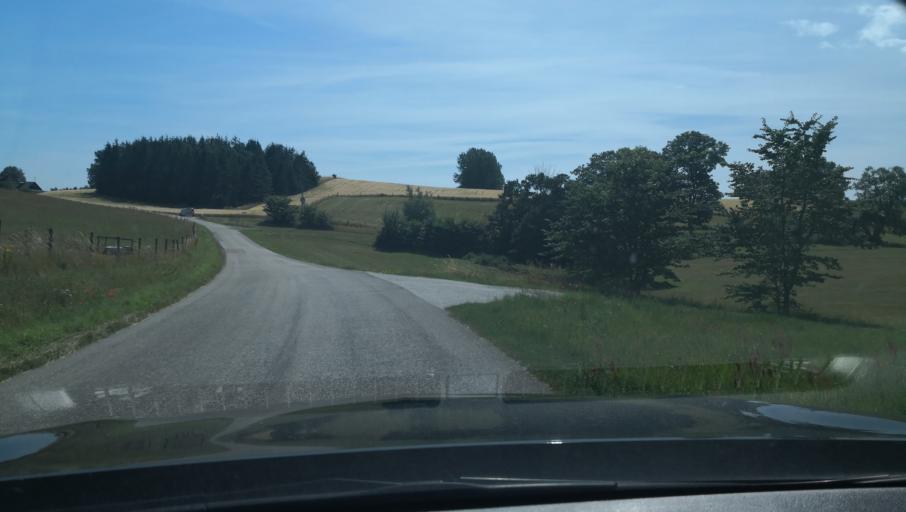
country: SE
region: Skane
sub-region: Ystads Kommun
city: Kopingebro
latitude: 55.3923
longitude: 14.1384
